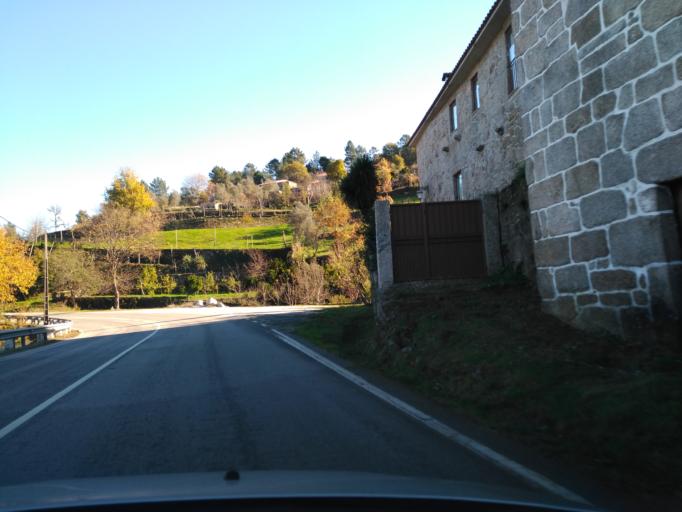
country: PT
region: Braga
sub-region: Vieira do Minho
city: Vieira do Minho
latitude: 41.6804
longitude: -8.1128
